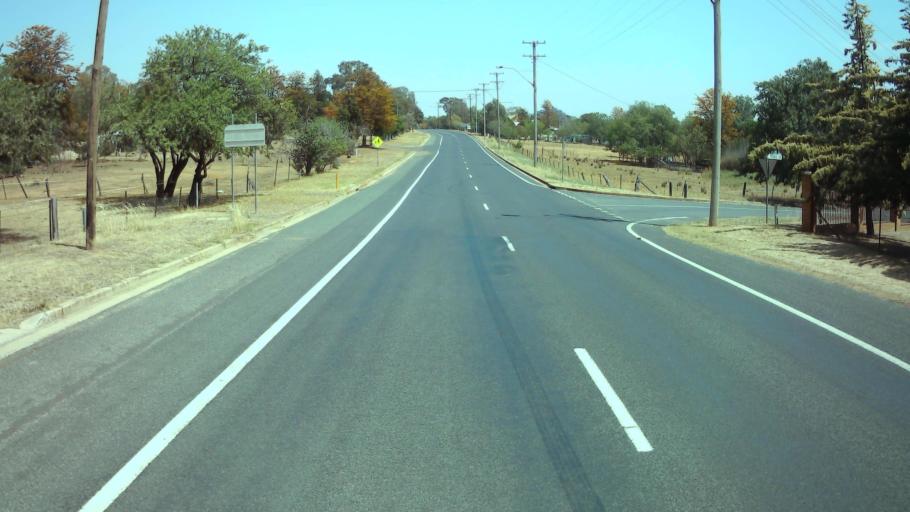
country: AU
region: New South Wales
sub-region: Weddin
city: Grenfell
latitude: -33.8965
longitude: 148.1724
